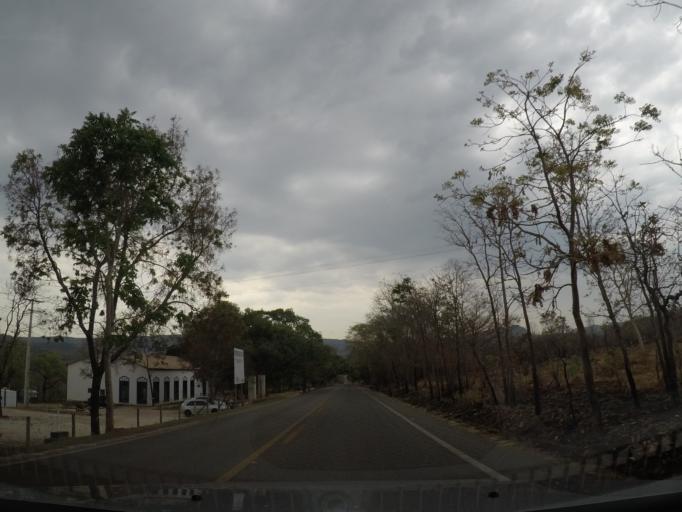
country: BR
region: Goias
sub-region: Pirenopolis
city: Pirenopolis
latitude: -15.8506
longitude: -48.9321
